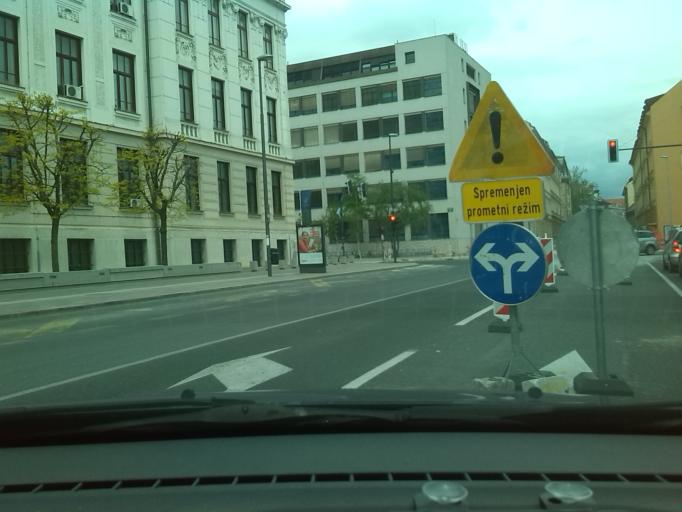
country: SI
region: Ljubljana
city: Ljubljana
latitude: 46.0457
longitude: 14.5009
